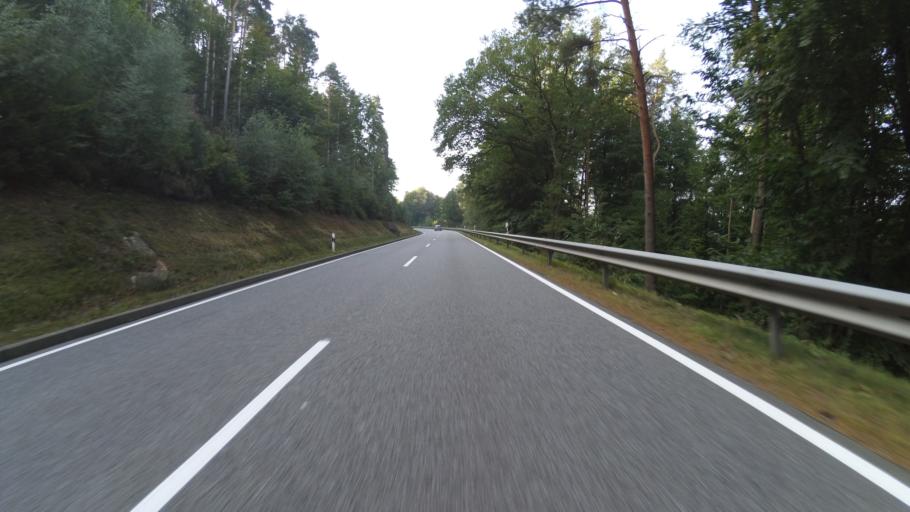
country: DE
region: Rheinland-Pfalz
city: Langwieden
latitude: 49.4040
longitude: 7.5231
